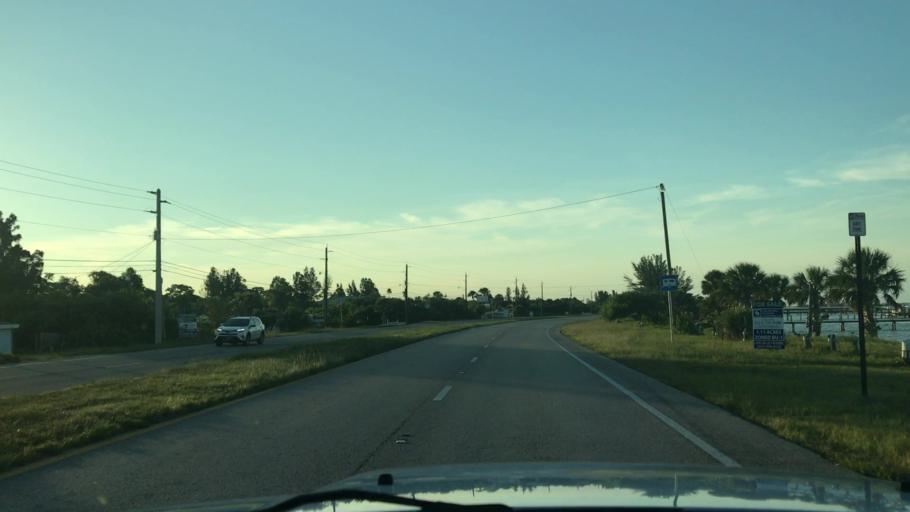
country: US
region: Florida
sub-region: Brevard County
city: Grant-Valkaria
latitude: 27.9568
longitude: -80.5386
